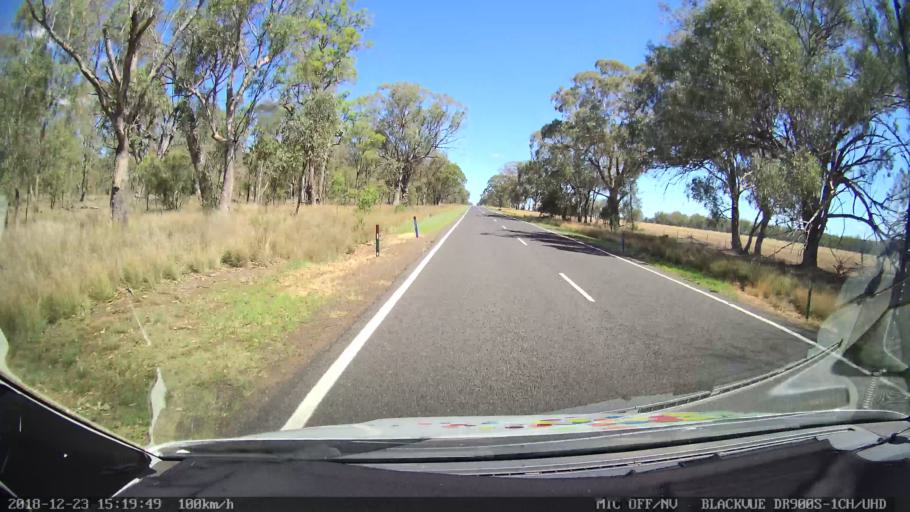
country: AU
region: New South Wales
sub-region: Tamworth Municipality
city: Manilla
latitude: -30.8341
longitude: 150.7854
